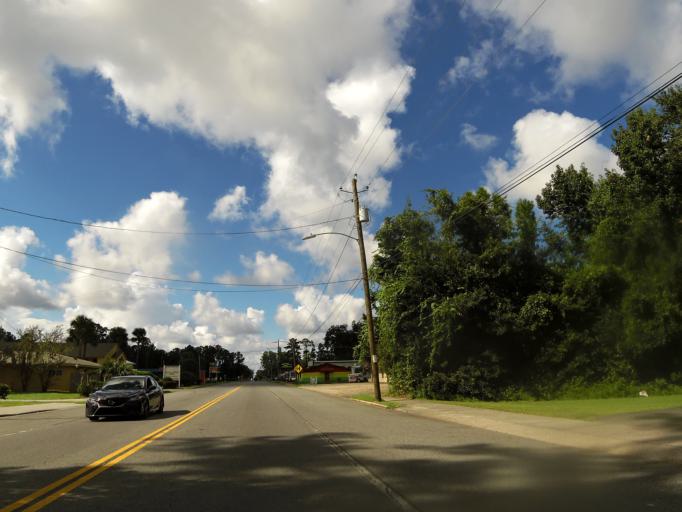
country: US
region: Georgia
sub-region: Camden County
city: Kingsland
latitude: 30.7928
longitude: -81.6888
